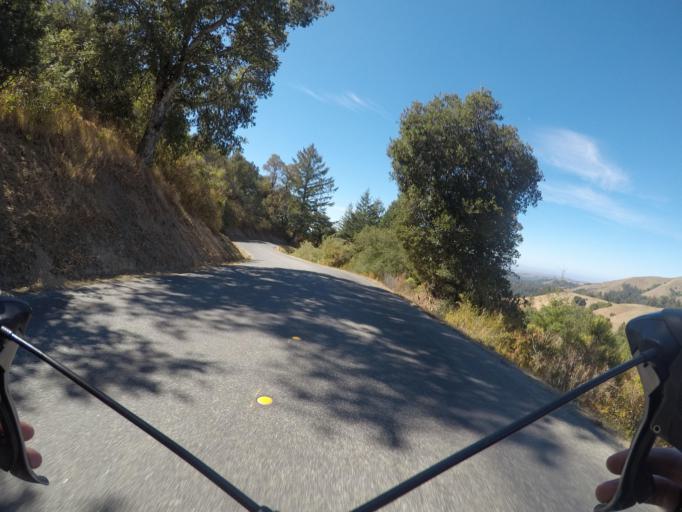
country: US
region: California
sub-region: San Mateo County
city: Portola Valley
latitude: 37.2947
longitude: -122.2096
